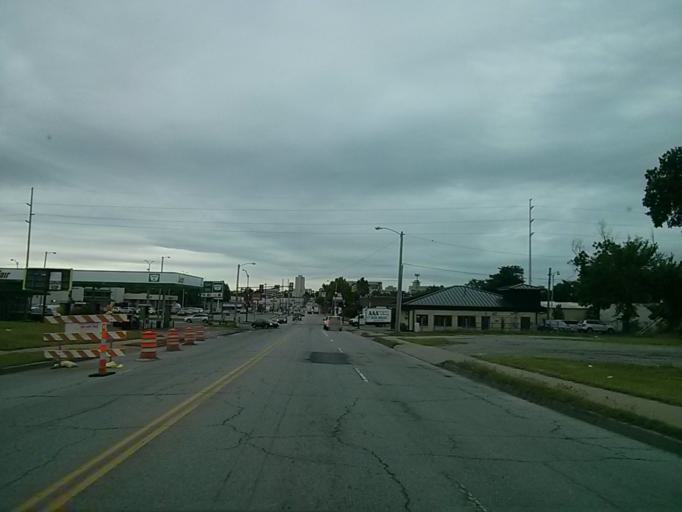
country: US
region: Oklahoma
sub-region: Tulsa County
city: Tulsa
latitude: 36.1576
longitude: -95.9671
